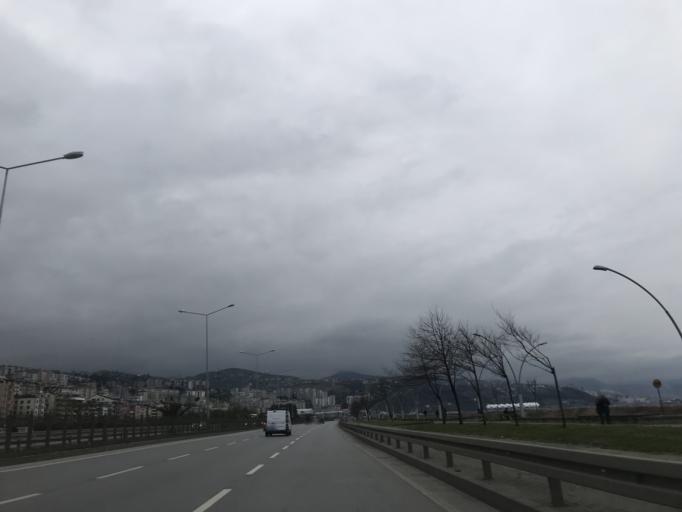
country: TR
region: Trabzon
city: Trabzon
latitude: 41.0004
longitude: 39.6829
